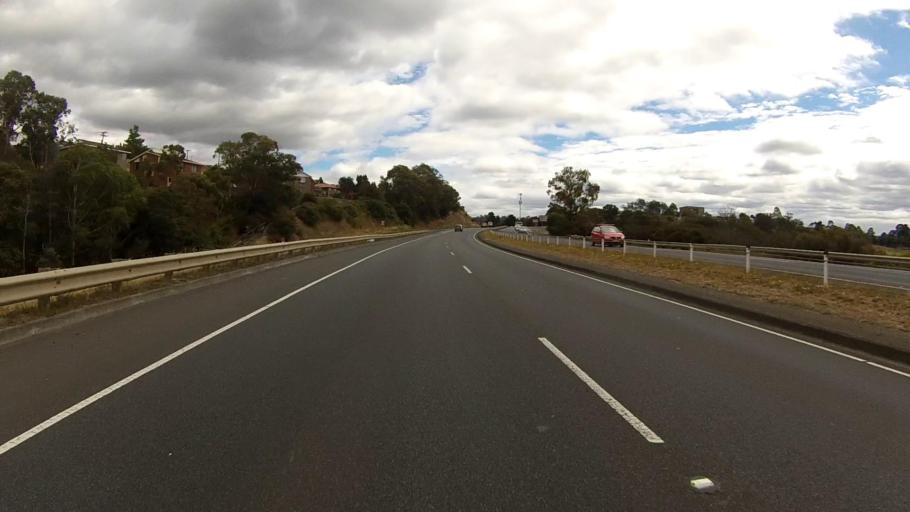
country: AU
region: Tasmania
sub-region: Glenorchy
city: Claremont
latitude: -42.7994
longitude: 147.2486
